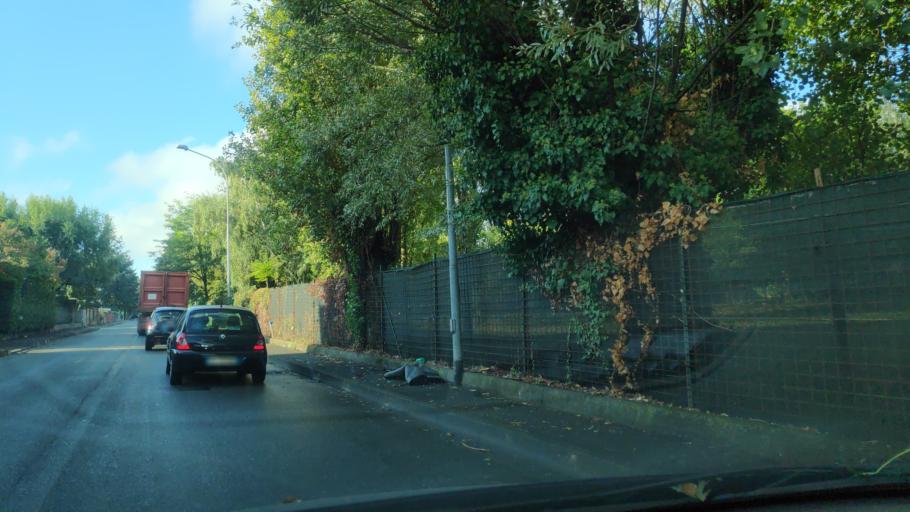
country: IT
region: Lombardy
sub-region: Citta metropolitana di Milano
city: Fizzonasco
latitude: 45.3753
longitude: 9.1886
